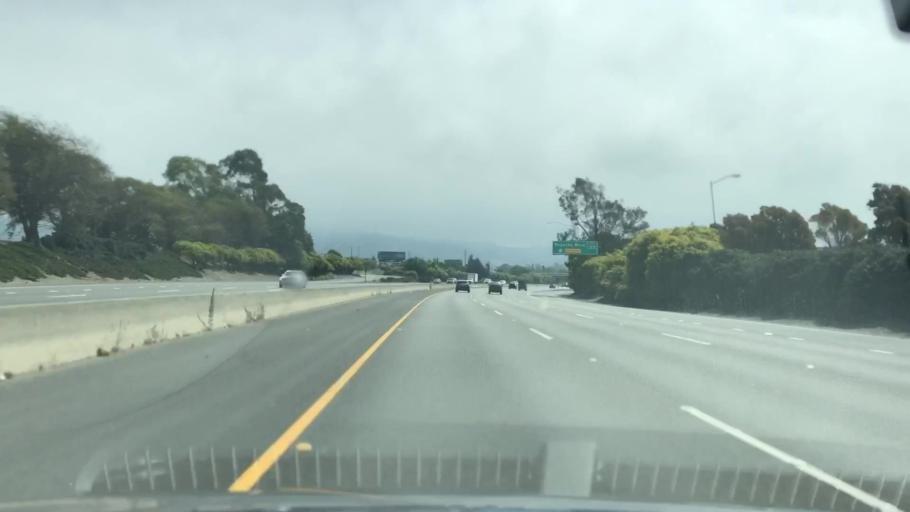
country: US
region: California
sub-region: Contra Costa County
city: Richmond
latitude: 37.9215
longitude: -122.3385
